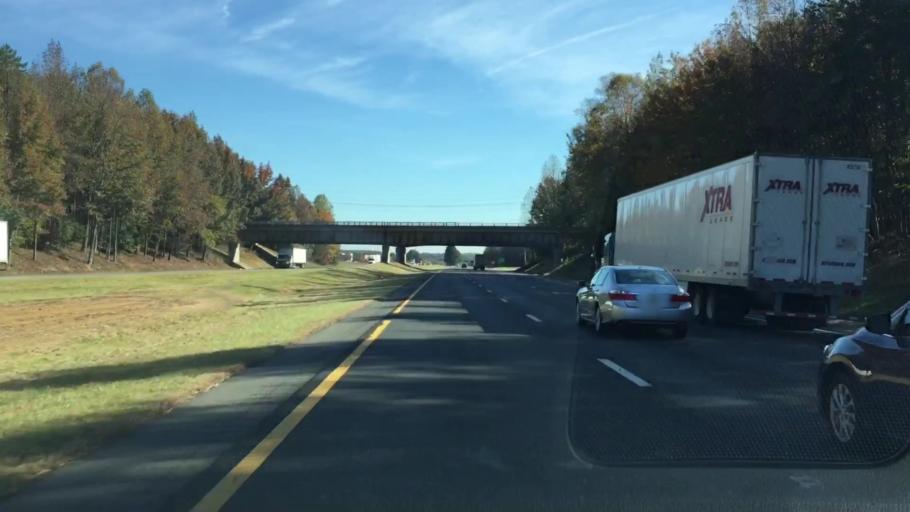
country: US
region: North Carolina
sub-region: Davidson County
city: Lexington
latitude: 35.7797
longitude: -80.2621
